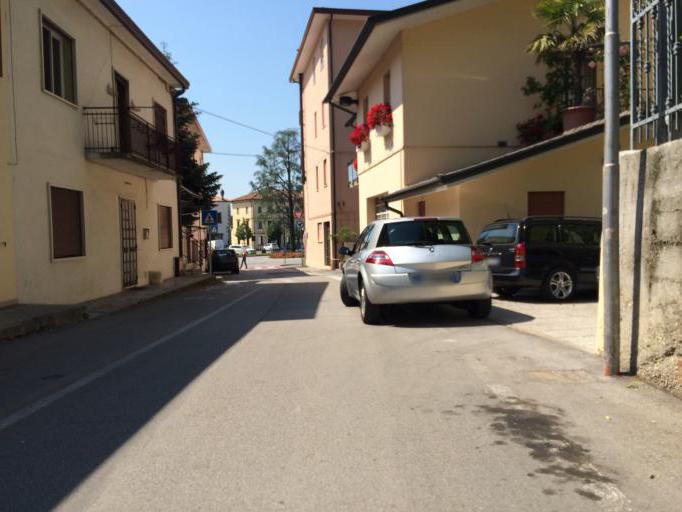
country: IT
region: Veneto
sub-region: Provincia di Vicenza
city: Montegalda
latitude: 45.4443
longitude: 11.6735
